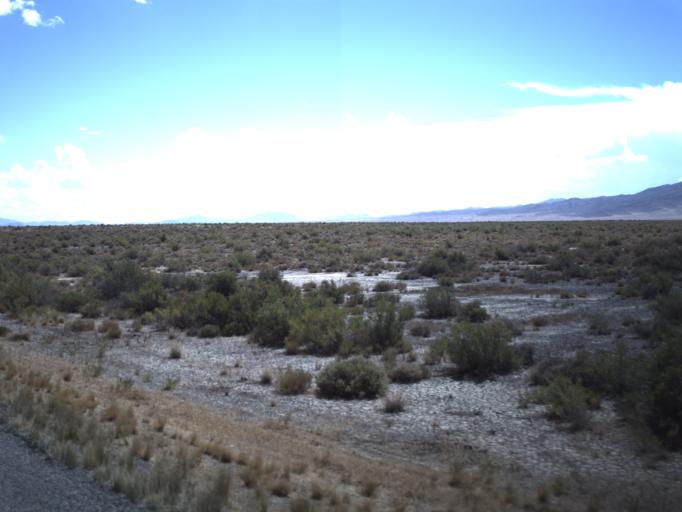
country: US
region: Nevada
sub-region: White Pine County
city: McGill
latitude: 39.0512
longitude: -113.9709
